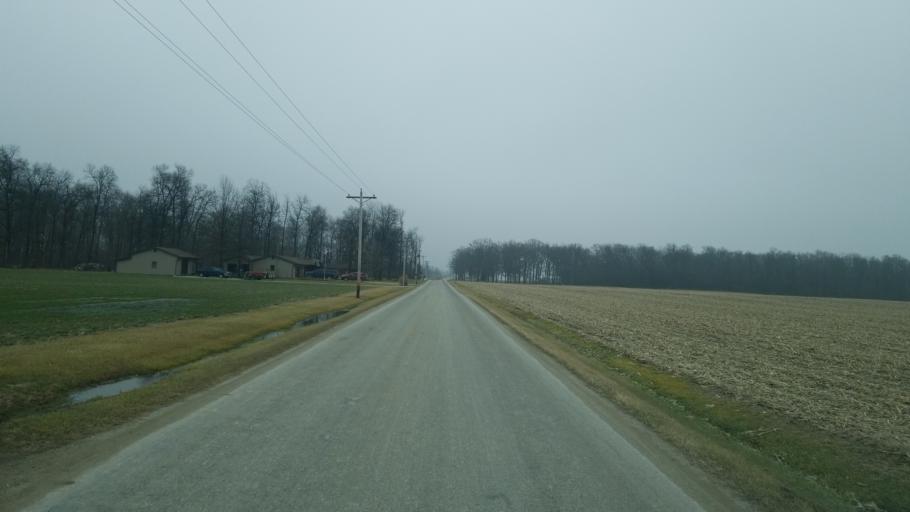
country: US
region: Indiana
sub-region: Adams County
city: Geneva
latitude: 40.5564
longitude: -84.9107
